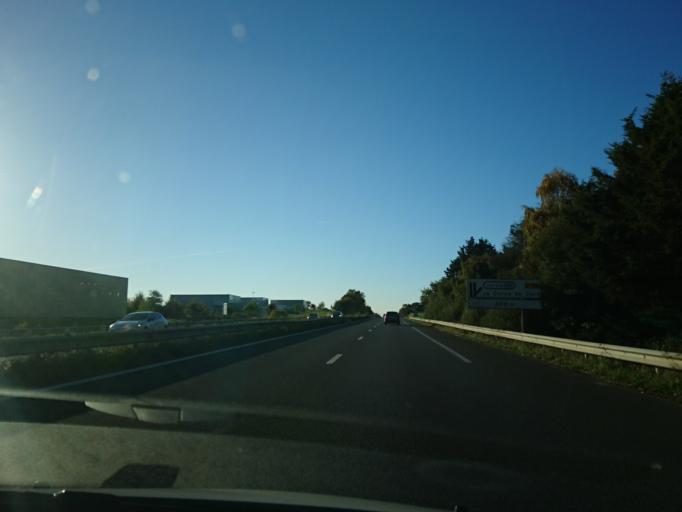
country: FR
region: Brittany
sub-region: Departement des Cotes-d'Armor
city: Lamballe
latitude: 48.4555
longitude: -2.5005
